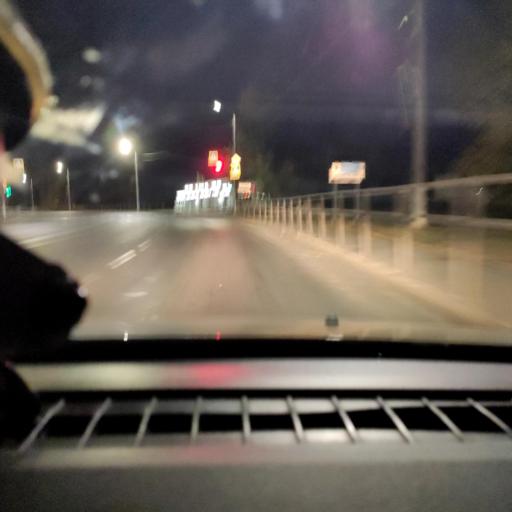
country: RU
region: Samara
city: Novokuybyshevsk
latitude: 53.0910
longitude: 49.9414
